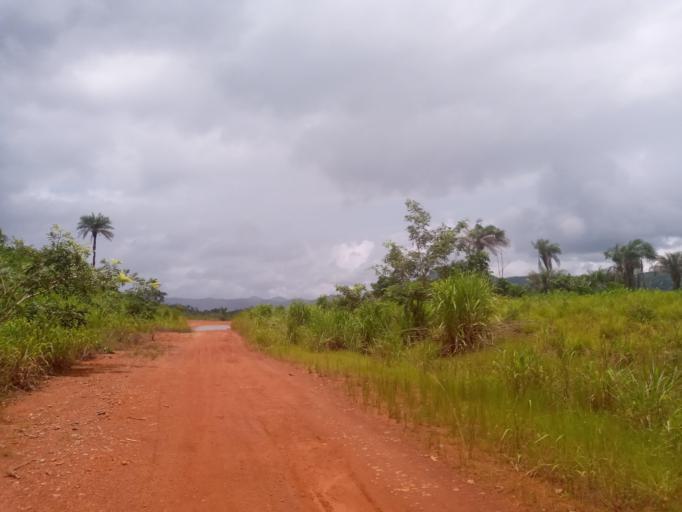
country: SL
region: Northern Province
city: Bumbuna
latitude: 8.9746
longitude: -11.7544
